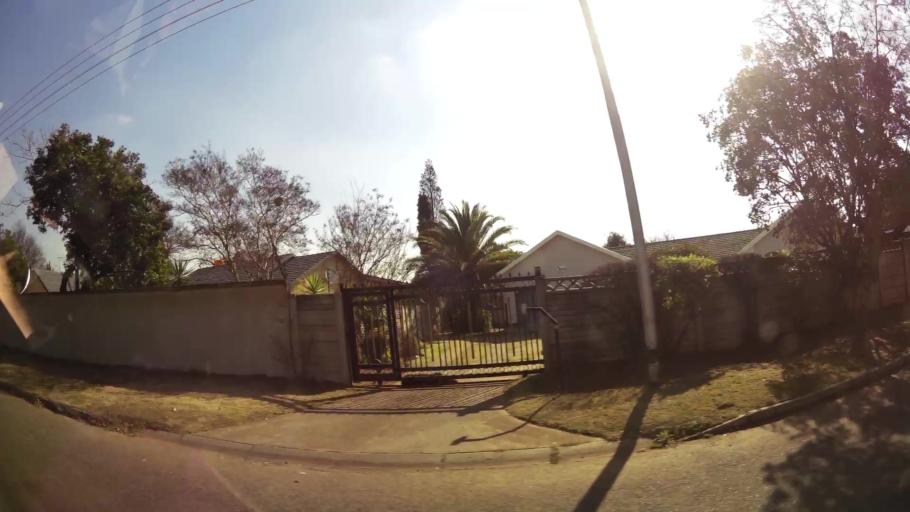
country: ZA
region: Gauteng
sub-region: West Rand District Municipality
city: Randfontein
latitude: -26.1516
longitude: 27.7051
